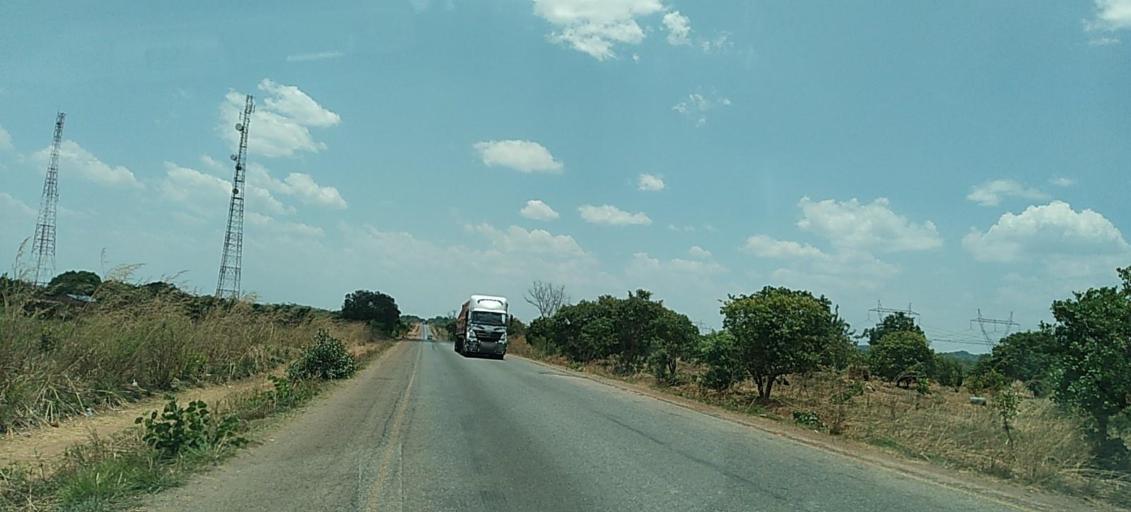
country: ZM
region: Central
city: Kapiri Mposhi
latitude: -13.6975
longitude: 28.6281
